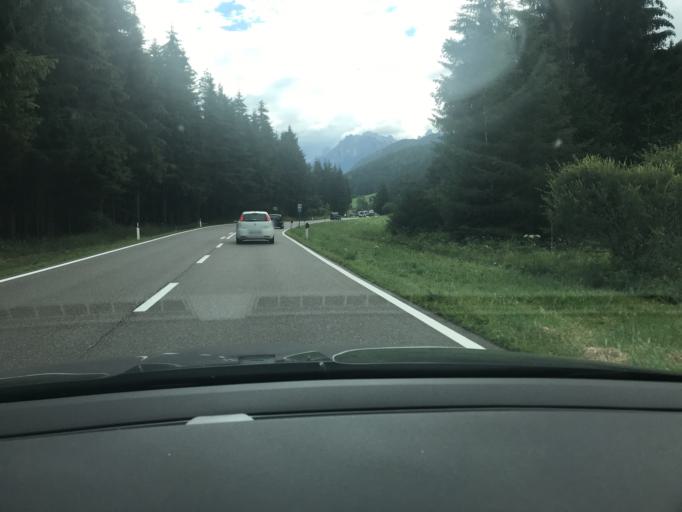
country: IT
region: Trentino-Alto Adige
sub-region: Bolzano
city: Villabassa
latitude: 46.7406
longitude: 12.1481
